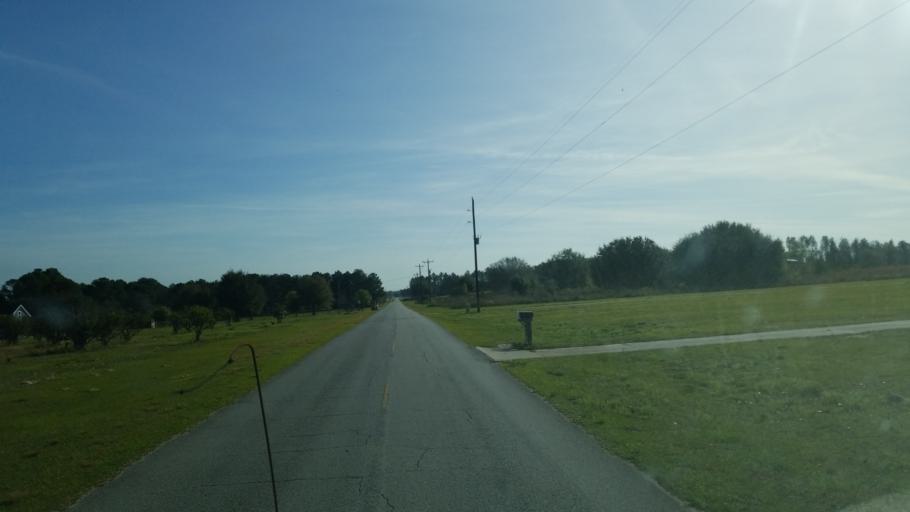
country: US
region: Florida
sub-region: Lake County
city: Clermont
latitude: 28.4615
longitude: -81.7786
